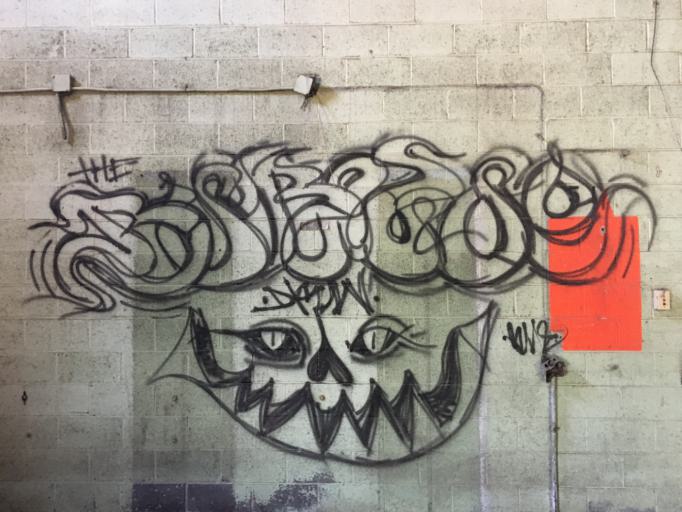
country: US
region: Michigan
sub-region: Wayne County
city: River Rouge
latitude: 42.3172
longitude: -83.1108
